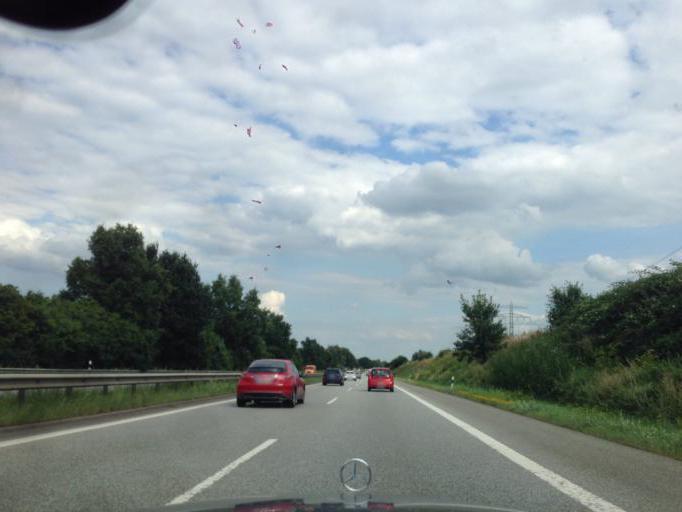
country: DE
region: Schleswig-Holstein
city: Oststeinbek
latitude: 53.4850
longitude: 10.1249
